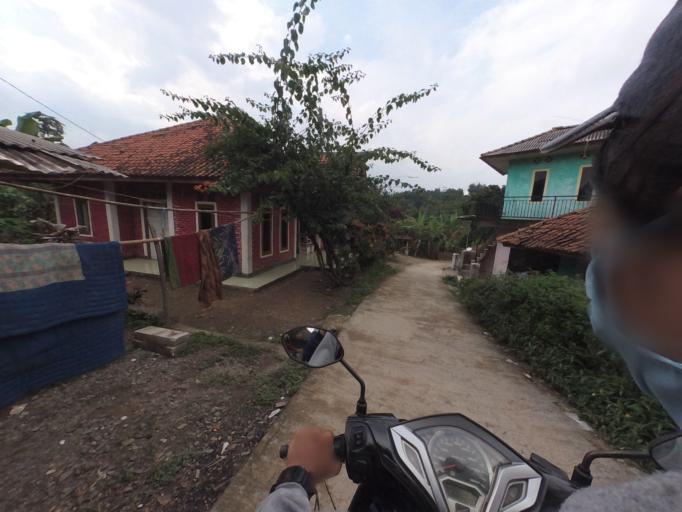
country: ID
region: West Java
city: Ciampea
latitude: -6.6847
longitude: 106.6594
